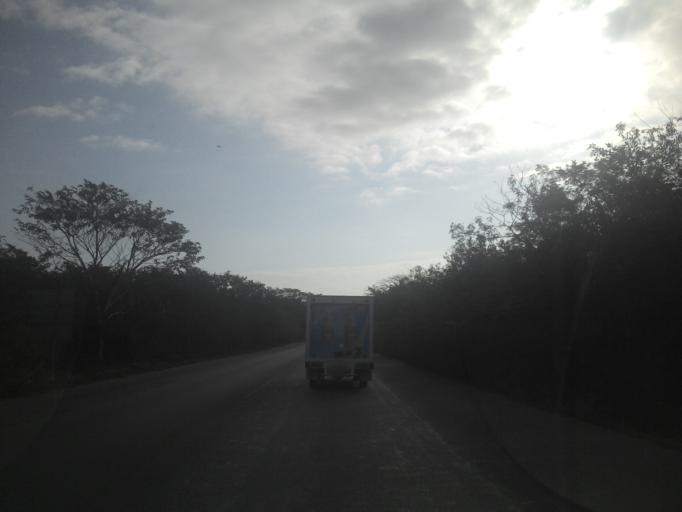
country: MX
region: Yucatan
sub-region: Valladolid
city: Tesoco
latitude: 20.7251
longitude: -88.1900
